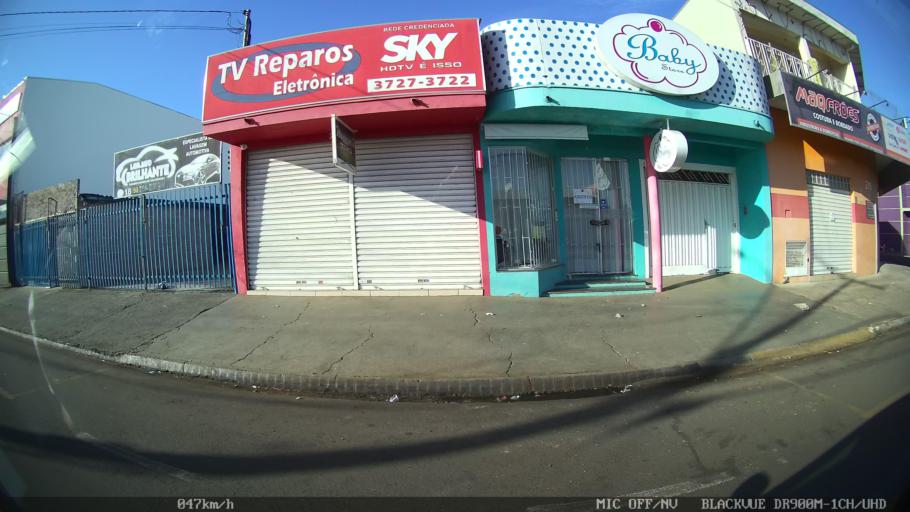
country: BR
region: Sao Paulo
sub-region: Franca
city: Franca
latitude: -20.5155
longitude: -47.3730
